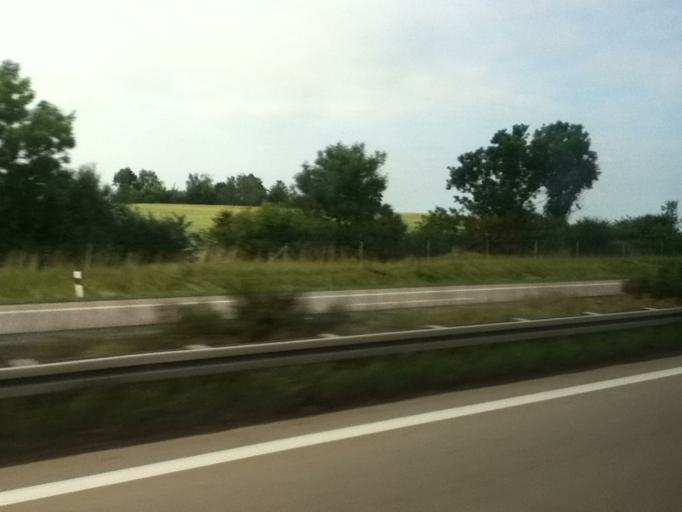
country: DE
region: Saxony
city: Klipphausen
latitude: 51.0603
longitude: 13.4608
